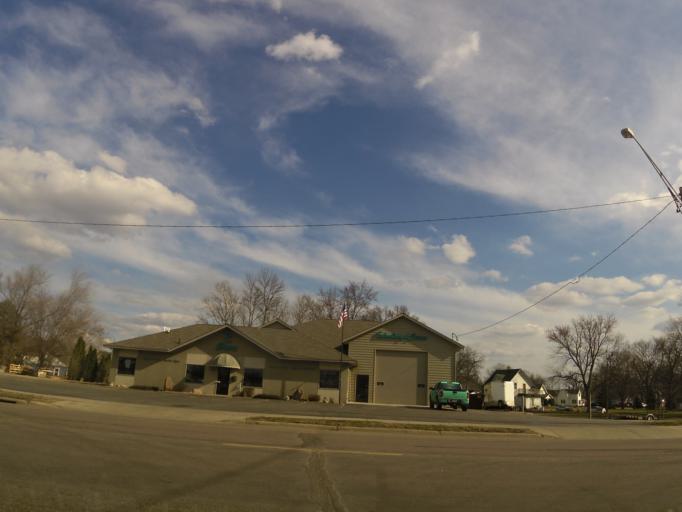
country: US
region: Minnesota
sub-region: Chippewa County
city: Montevideo
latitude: 44.9388
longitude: -95.7242
